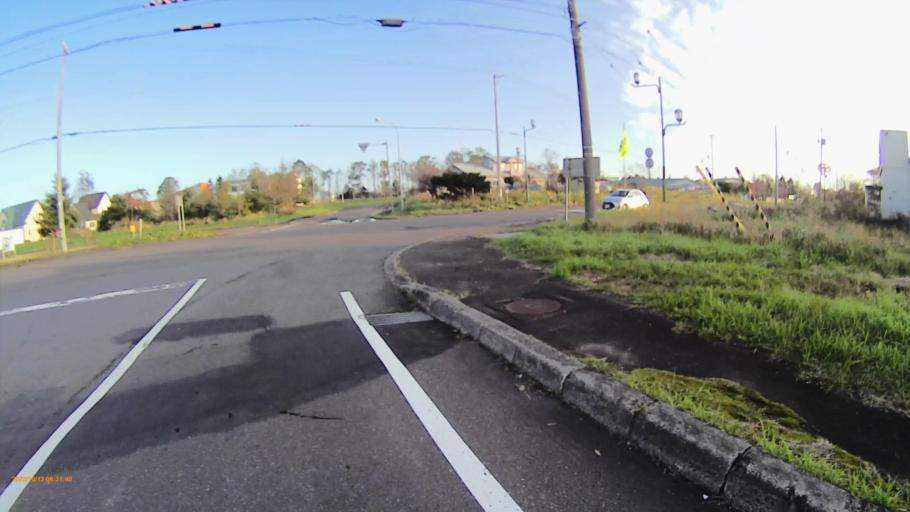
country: JP
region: Hokkaido
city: Kushiro
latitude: 42.8902
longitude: 143.9362
